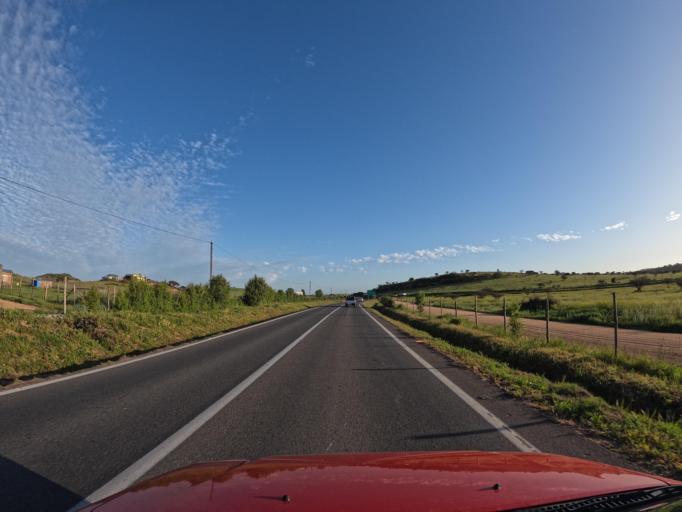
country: CL
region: O'Higgins
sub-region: Provincia de Colchagua
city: Santa Cruz
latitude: -34.2038
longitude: -71.7360
